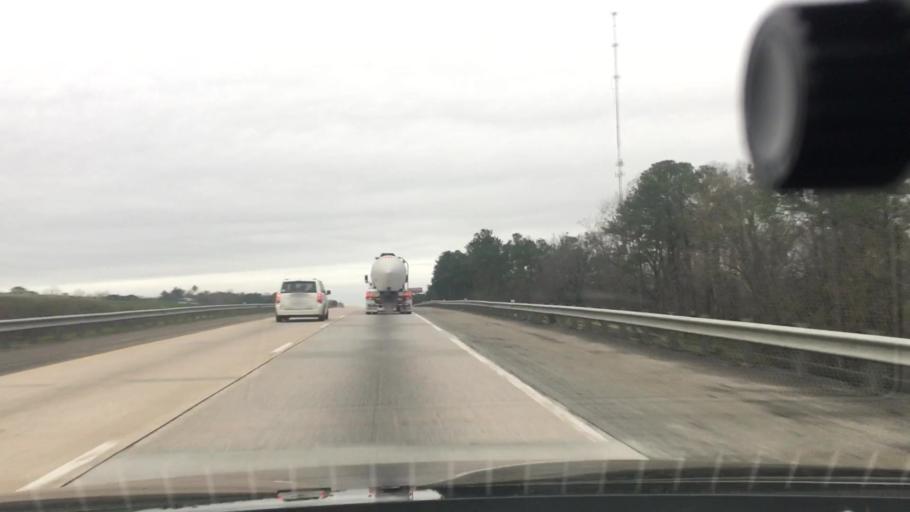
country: US
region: Georgia
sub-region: Monroe County
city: Forsyth
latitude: 32.9574
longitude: -83.8110
